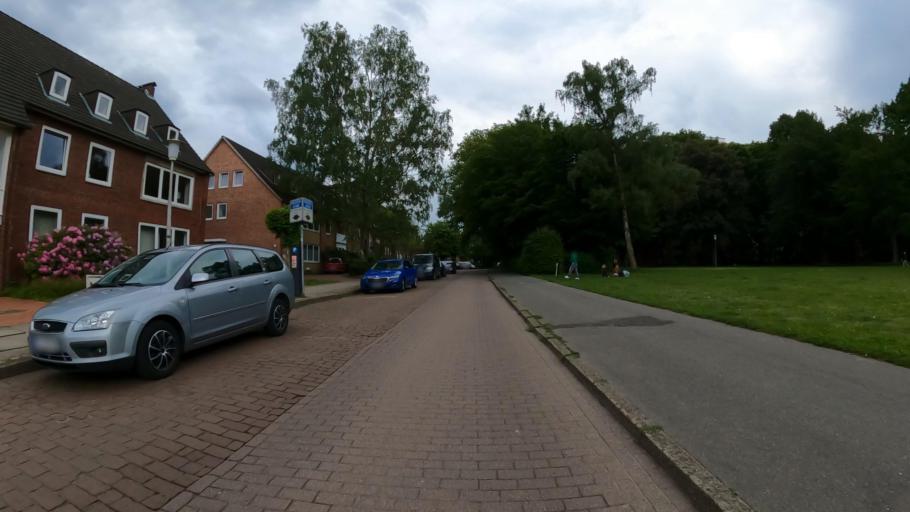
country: DE
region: Schleswig-Holstein
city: Pinneberg
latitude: 53.6601
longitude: 9.7972
